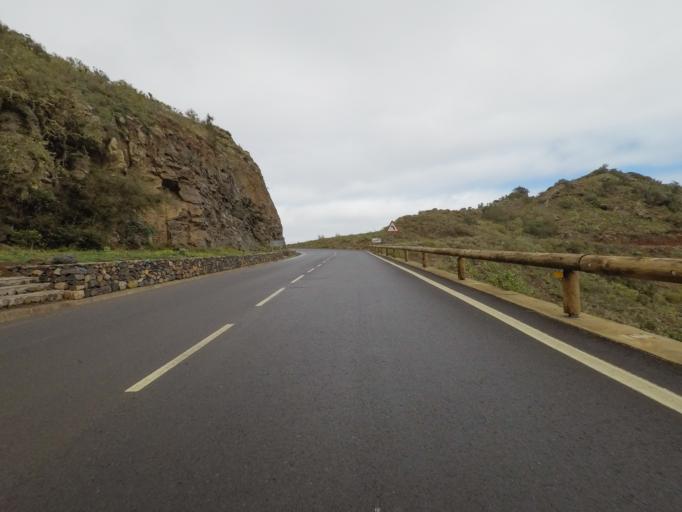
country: ES
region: Canary Islands
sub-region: Provincia de Santa Cruz de Tenerife
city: Agulo
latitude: 28.1893
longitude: -17.2207
